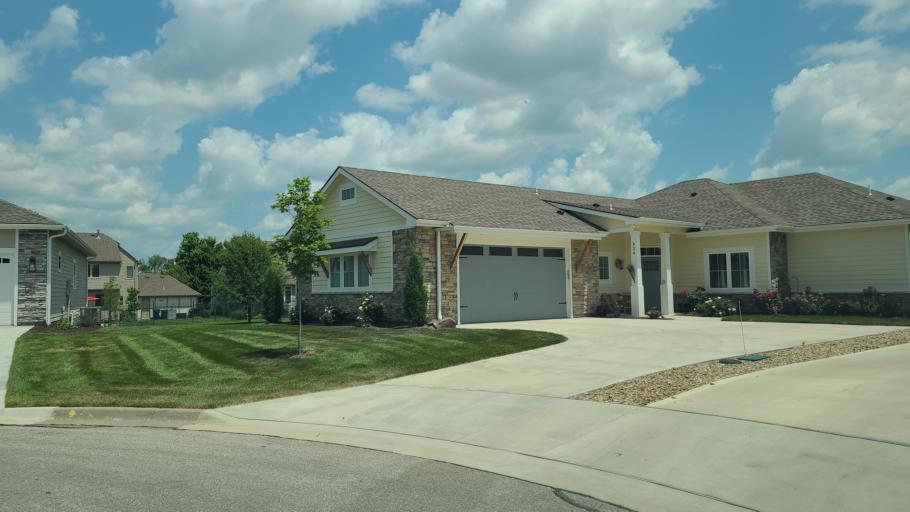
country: US
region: Kansas
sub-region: Douglas County
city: Lawrence
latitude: 38.9838
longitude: -95.3121
